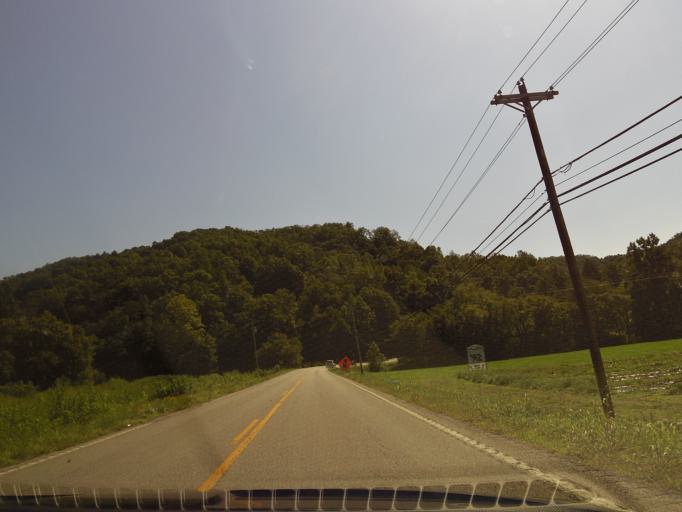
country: US
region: Kentucky
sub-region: Clay County
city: Manchester
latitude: 37.0894
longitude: -83.6929
